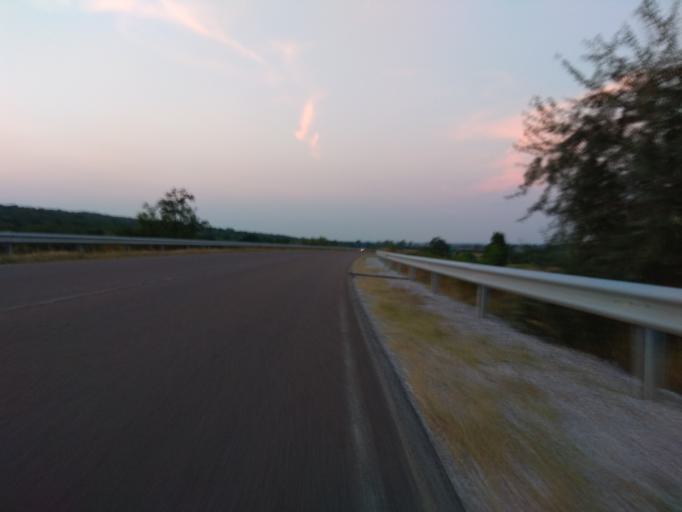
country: HU
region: Borsod-Abauj-Zemplen
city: Emod
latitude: 47.9376
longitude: 20.8276
